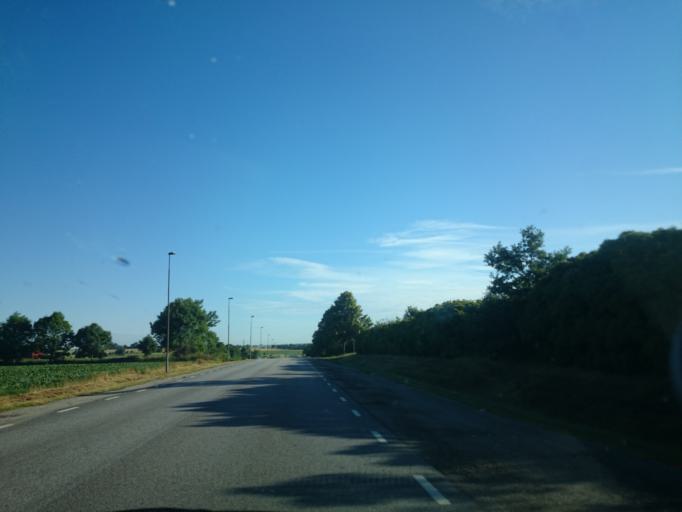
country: SE
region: Skane
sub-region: Eslovs Kommun
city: Eslov
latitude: 55.7182
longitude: 13.3315
